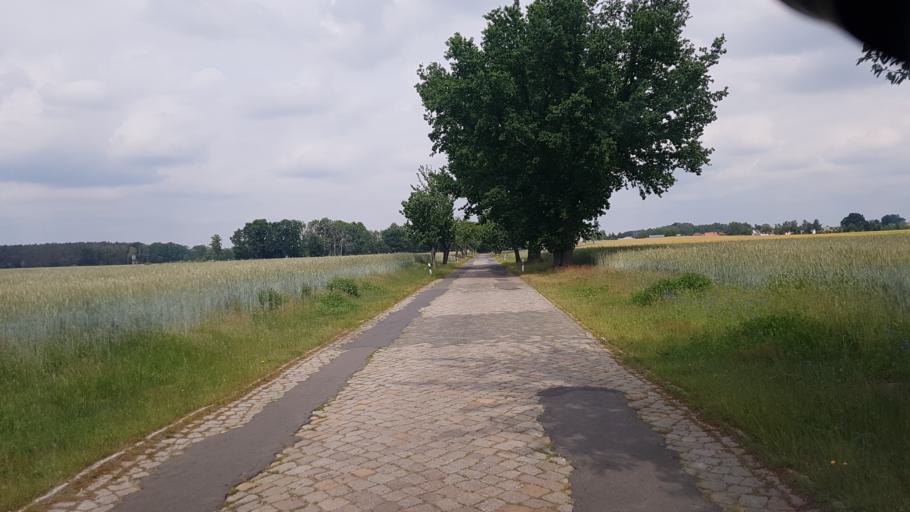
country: DE
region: Brandenburg
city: Lebusa
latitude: 51.8059
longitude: 13.4484
